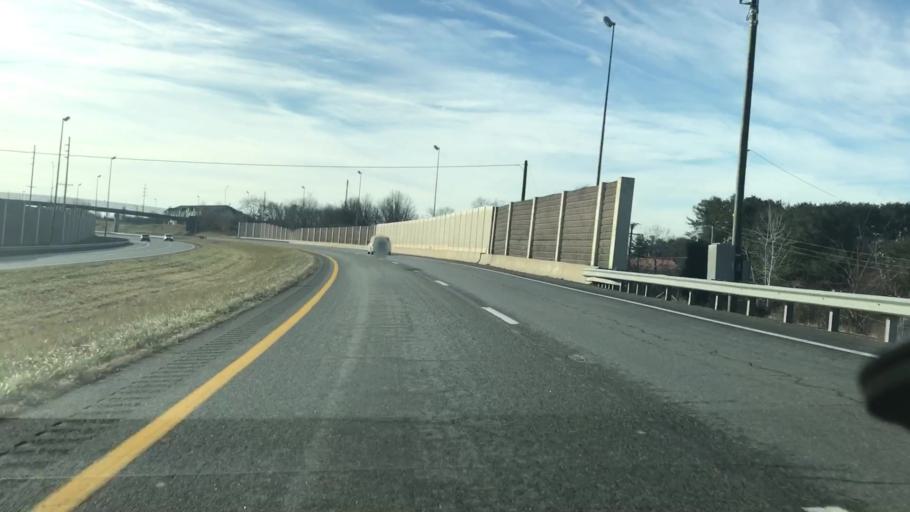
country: US
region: Virginia
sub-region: Montgomery County
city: Merrimac
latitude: 37.1736
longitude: -80.4168
